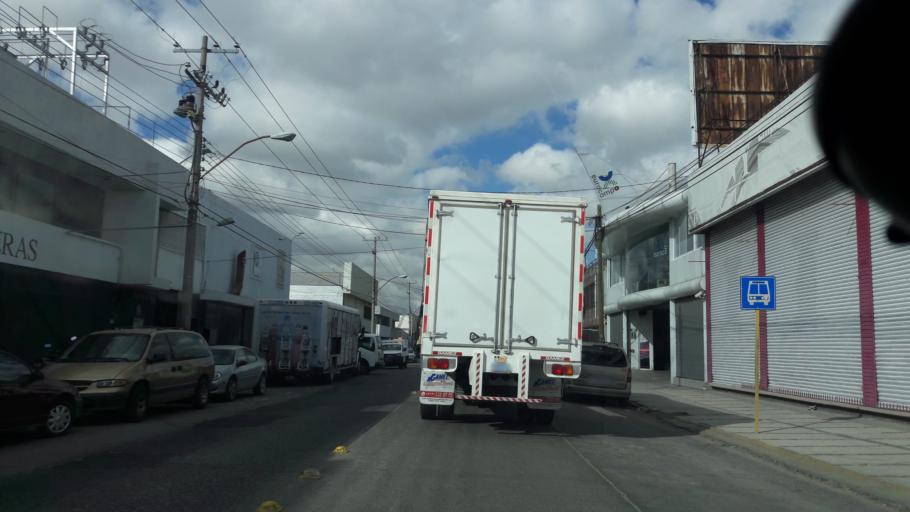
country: MX
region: Guanajuato
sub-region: Leon
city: Medina
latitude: 21.1041
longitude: -101.6295
